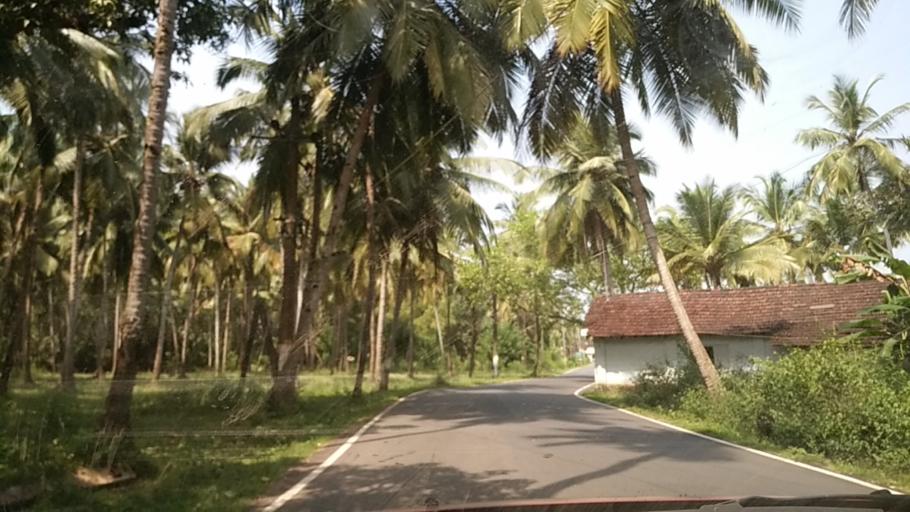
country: IN
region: Goa
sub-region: South Goa
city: Colva
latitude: 15.3118
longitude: 73.9153
